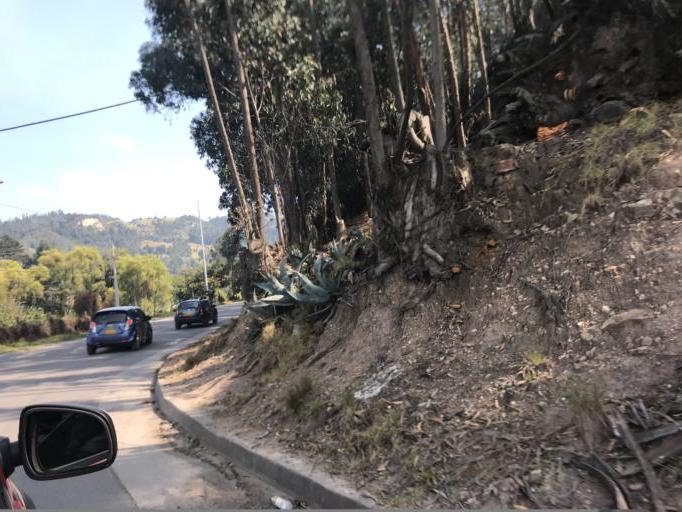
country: CO
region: Boyaca
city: Samaca
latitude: 5.4911
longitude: -73.4792
